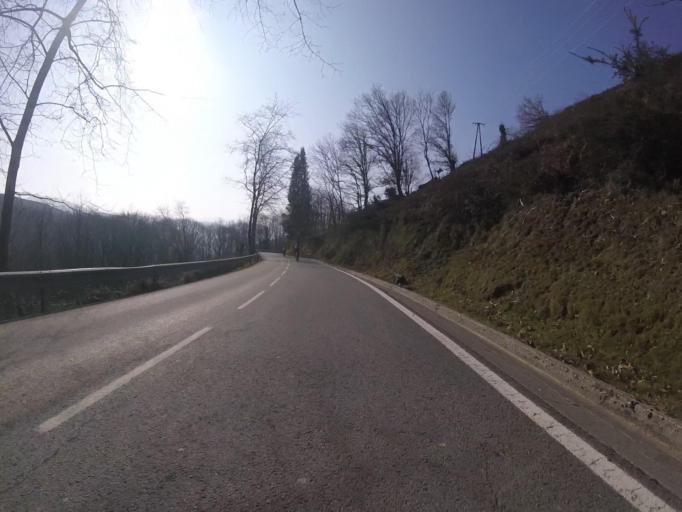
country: ES
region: Navarre
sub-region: Provincia de Navarra
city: Bera
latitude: 43.3024
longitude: -1.6895
